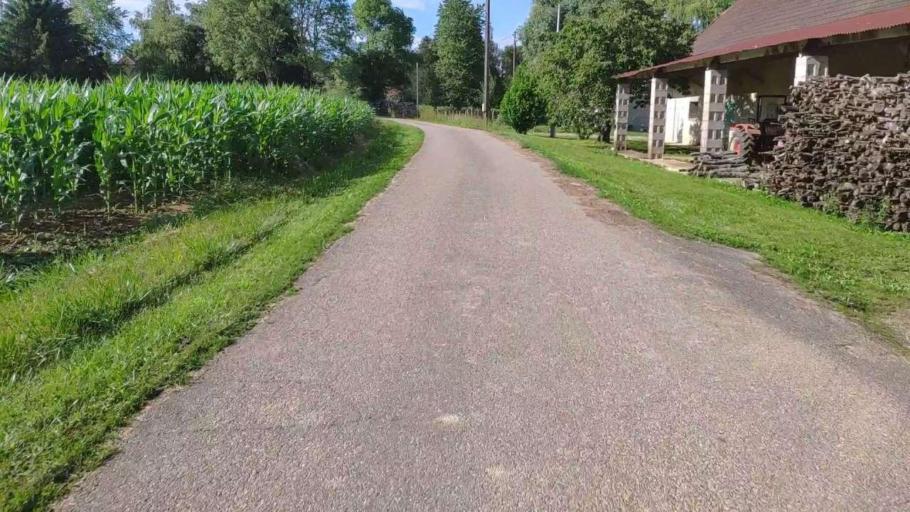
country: FR
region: Franche-Comte
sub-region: Departement du Jura
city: Bletterans
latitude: 46.8127
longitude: 5.4961
